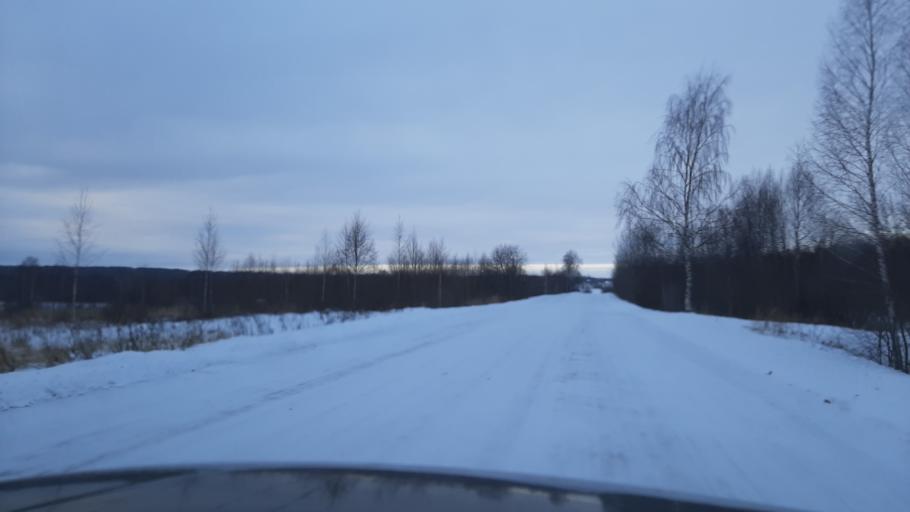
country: RU
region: Kostroma
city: Volgorechensk
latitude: 57.4474
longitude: 40.9931
